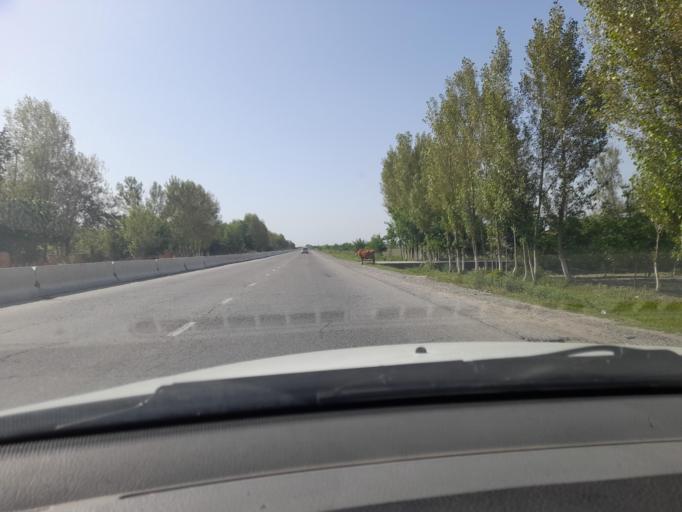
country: UZ
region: Samarqand
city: Daxbet
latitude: 39.8158
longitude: 66.8501
